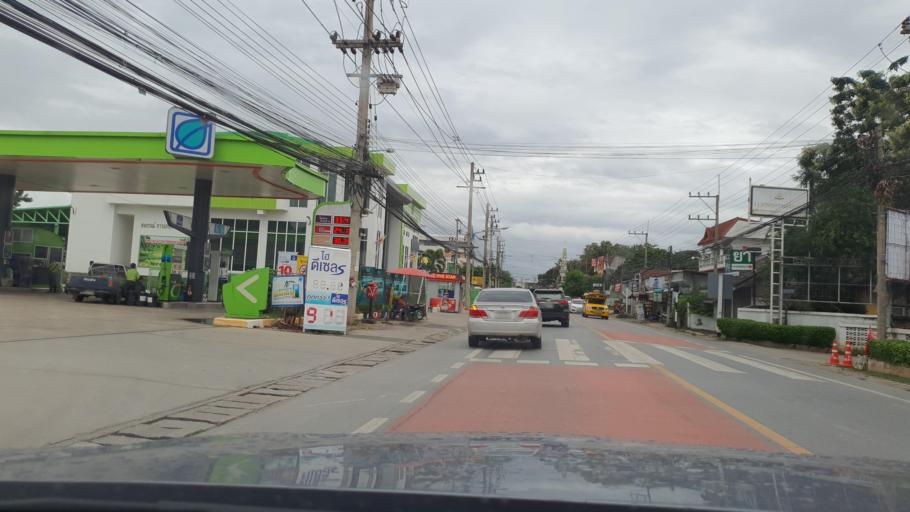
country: TH
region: Chiang Mai
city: Hang Dong
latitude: 18.6804
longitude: 98.9180
